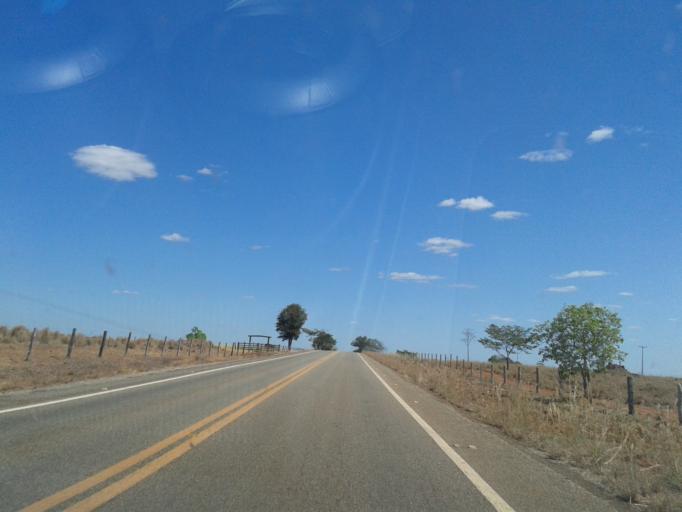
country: BR
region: Goias
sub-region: Sao Miguel Do Araguaia
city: Sao Miguel do Araguaia
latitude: -13.4031
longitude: -50.2601
